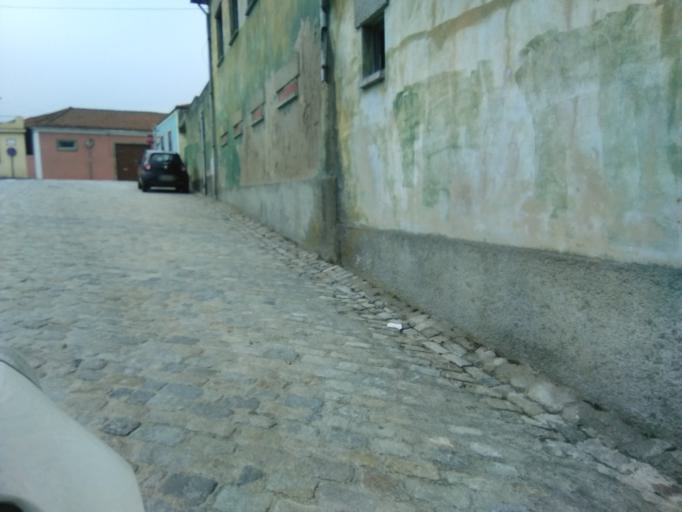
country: PT
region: Porto
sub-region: Matosinhos
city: Santa Cruz do Bispo
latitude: 41.2252
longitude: -8.7040
